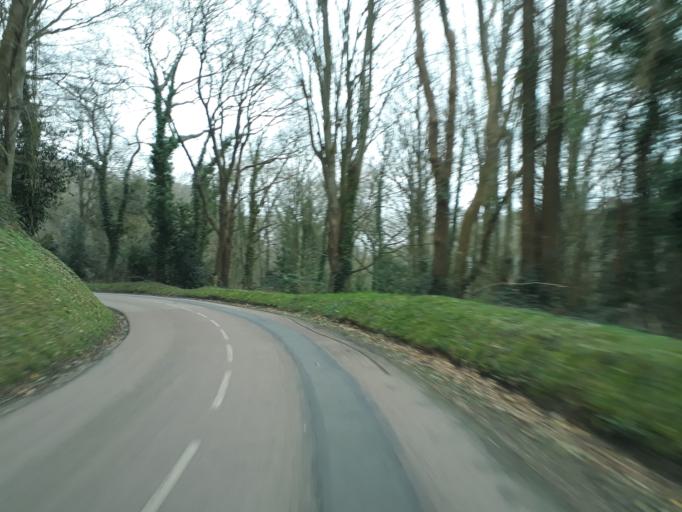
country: FR
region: Haute-Normandie
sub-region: Departement de la Seine-Maritime
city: Yport
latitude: 49.7318
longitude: 0.2902
